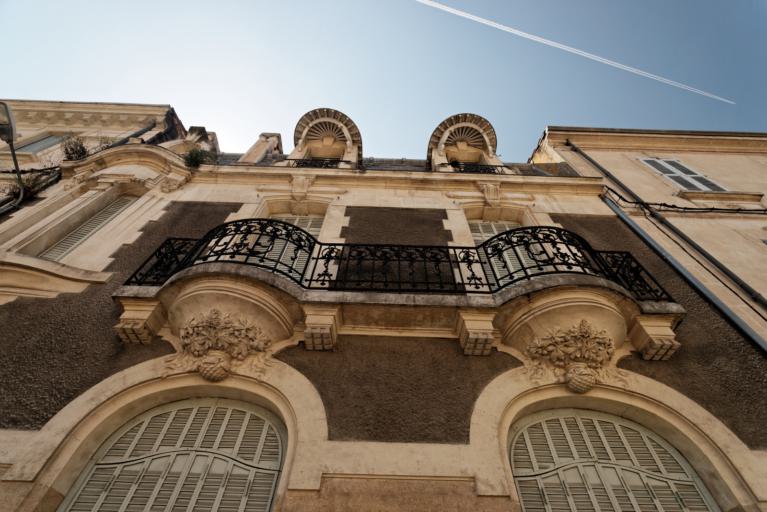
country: FR
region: Provence-Alpes-Cote d'Azur
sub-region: Departement du Vaucluse
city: Avignon
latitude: 43.9489
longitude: 4.8145
